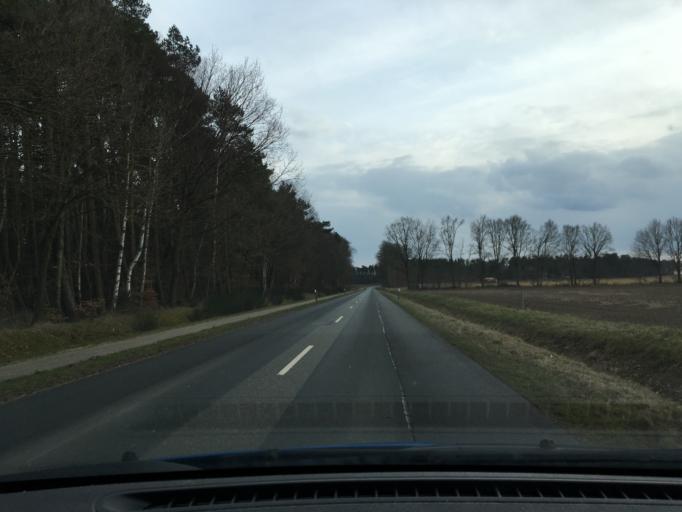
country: DE
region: Lower Saxony
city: Reppenstedt
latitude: 53.2665
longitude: 10.3417
